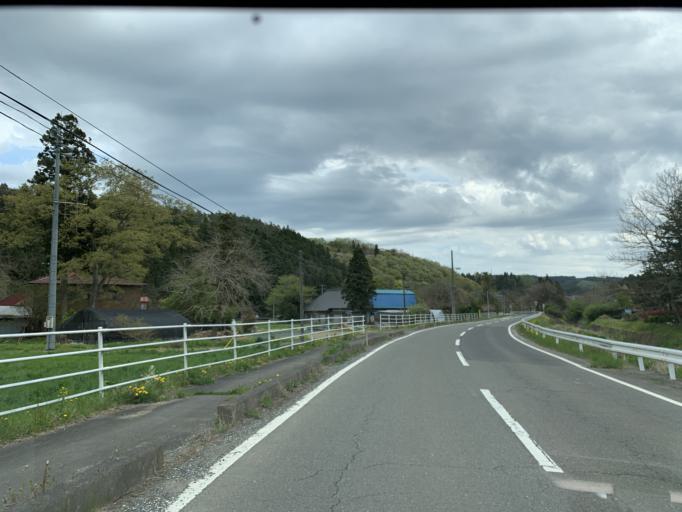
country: JP
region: Iwate
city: Ichinoseki
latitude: 38.7814
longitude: 141.3278
